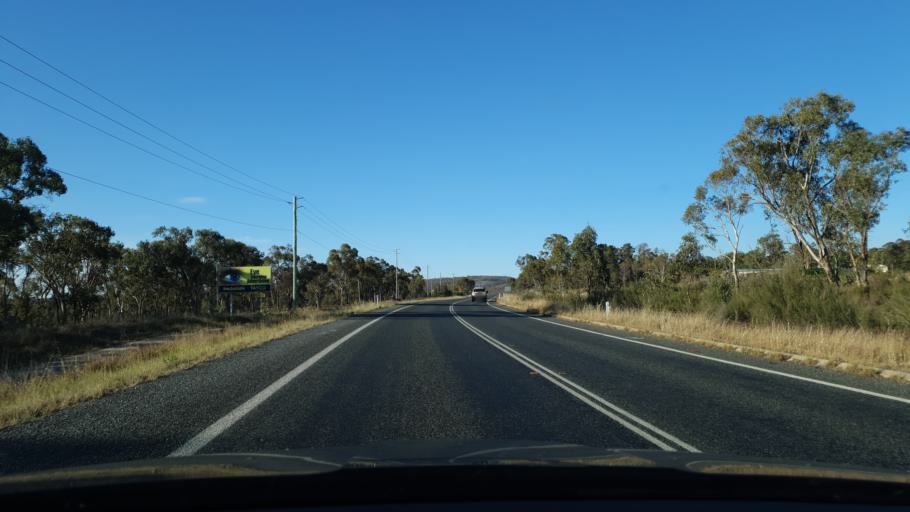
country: AU
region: Queensland
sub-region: Southern Downs
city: Stanthorpe
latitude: -28.6659
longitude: 151.9154
